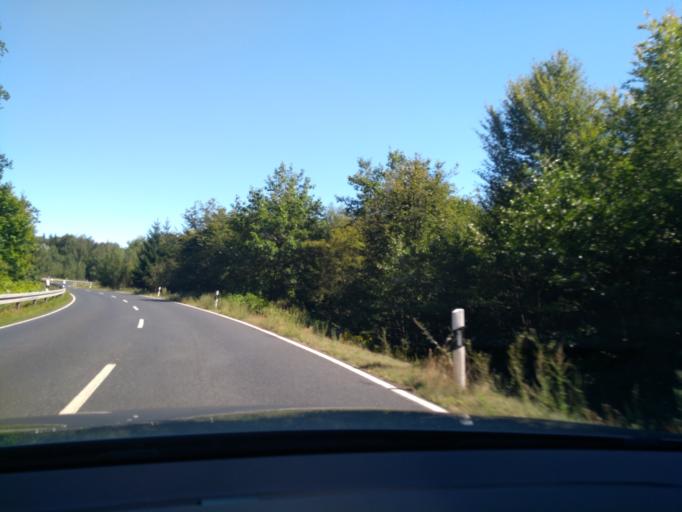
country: DE
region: Saxony
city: Arnsdorf
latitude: 51.1360
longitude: 13.9820
